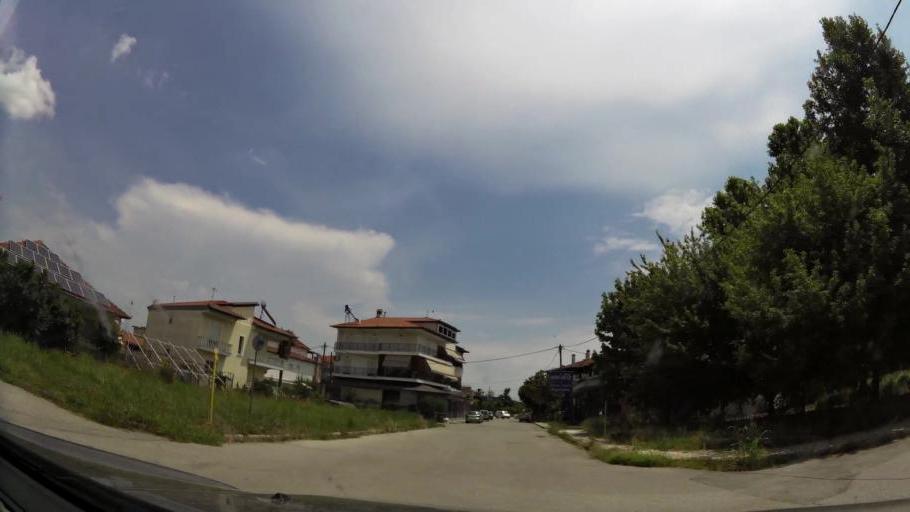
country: GR
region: Central Macedonia
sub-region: Nomos Pierias
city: Peristasi
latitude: 40.2719
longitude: 22.5304
